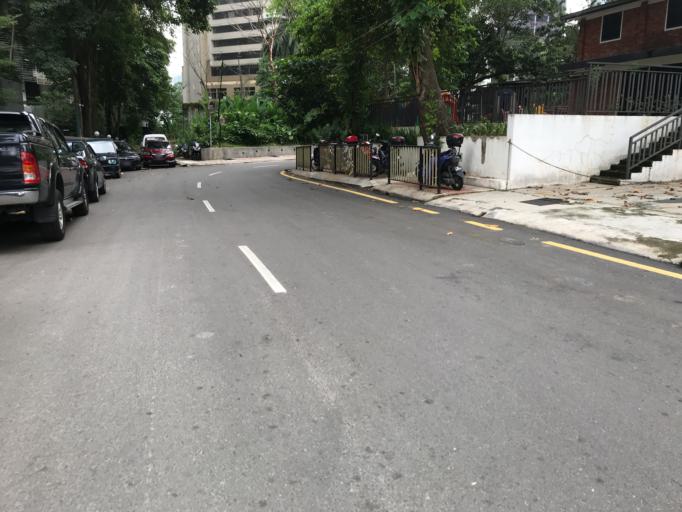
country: MY
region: Kuala Lumpur
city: Kuala Lumpur
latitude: 3.1608
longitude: 101.7132
